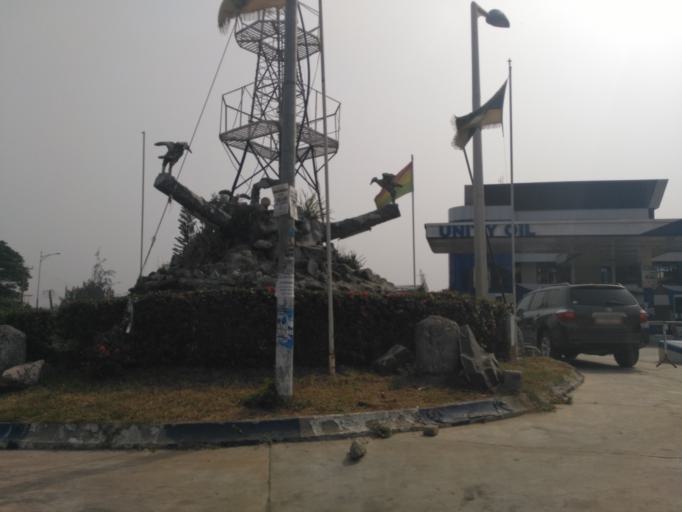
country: GH
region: Ashanti
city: Kumasi
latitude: 6.6804
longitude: -1.6041
